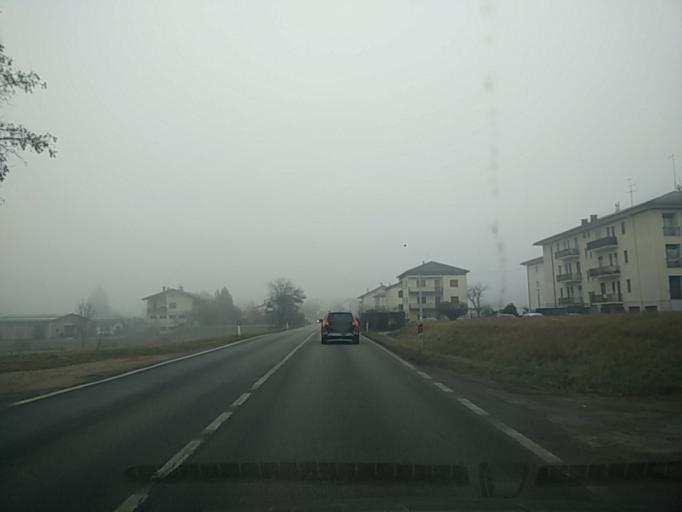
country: IT
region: Veneto
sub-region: Provincia di Belluno
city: Villabruna-Umin
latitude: 46.0271
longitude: 11.9364
